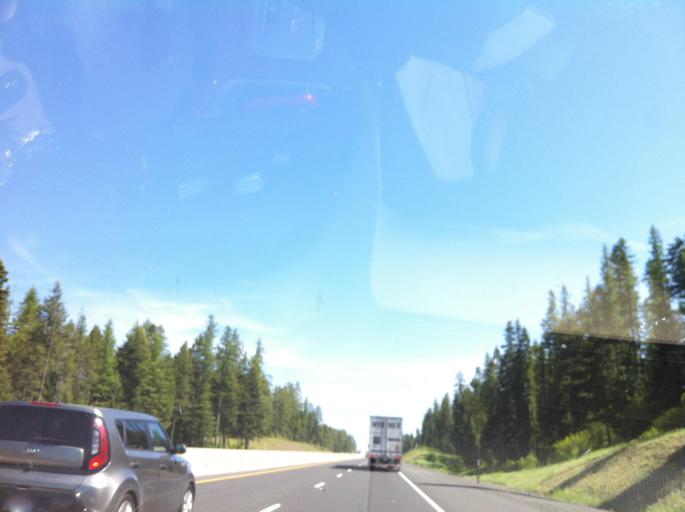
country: US
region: Oregon
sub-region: Umatilla County
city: Mission
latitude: 45.4875
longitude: -118.4088
